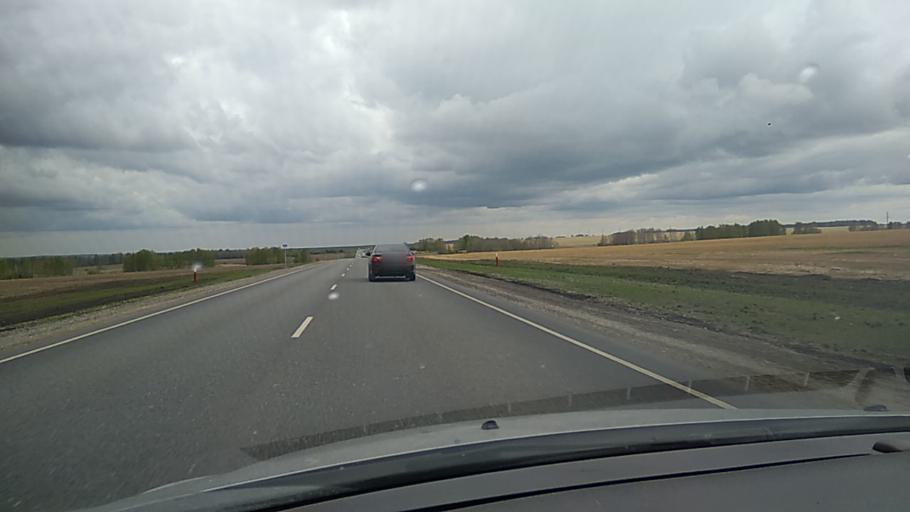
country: RU
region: Kurgan
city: Dalmatovo
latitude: 56.2890
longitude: 62.7718
